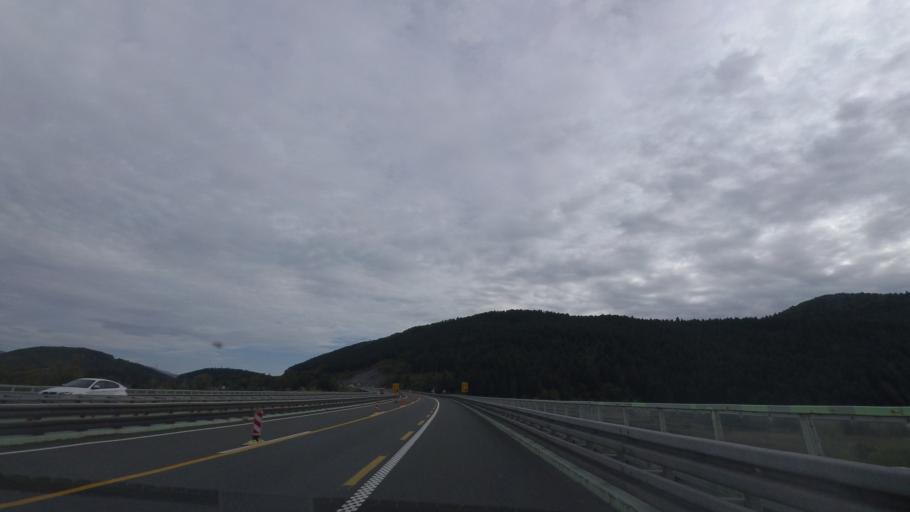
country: HR
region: Licko-Senjska
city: Otocac
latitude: 44.8641
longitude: 15.2091
